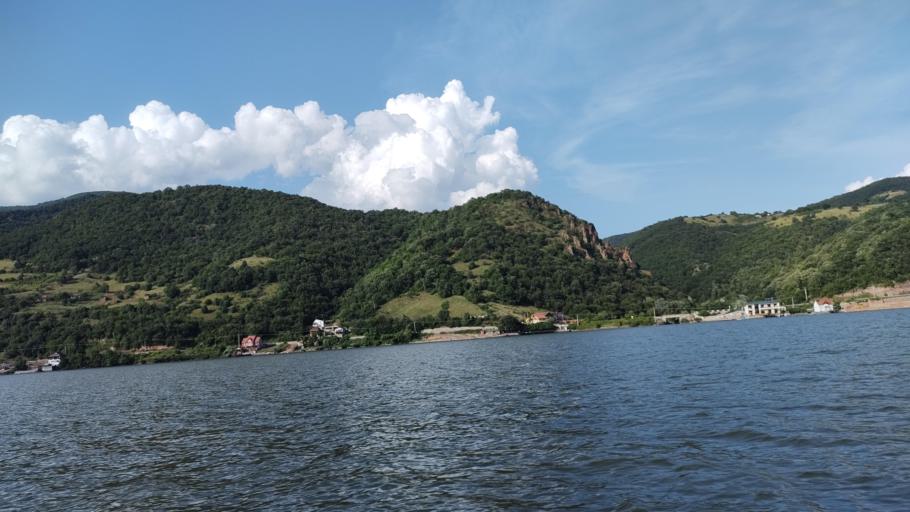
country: RO
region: Mehedinti
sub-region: Comuna Svinita
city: Svinita
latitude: 44.5373
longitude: 22.0586
